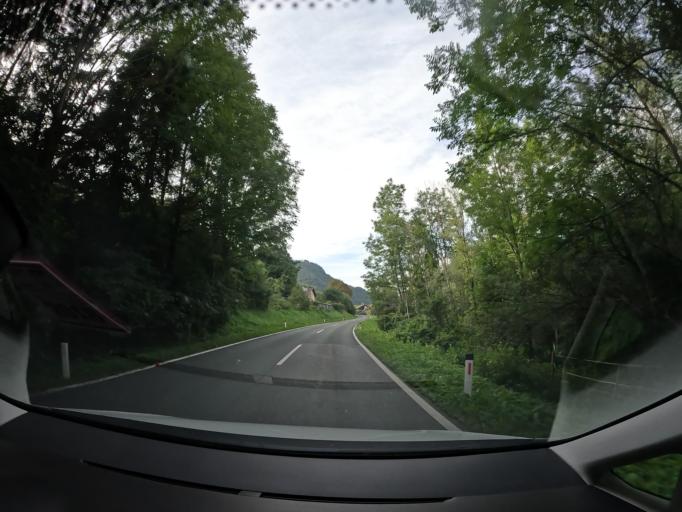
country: AT
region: Carinthia
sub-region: Politischer Bezirk Volkermarkt
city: Bad Eisenkappel
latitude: 46.5012
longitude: 14.5770
